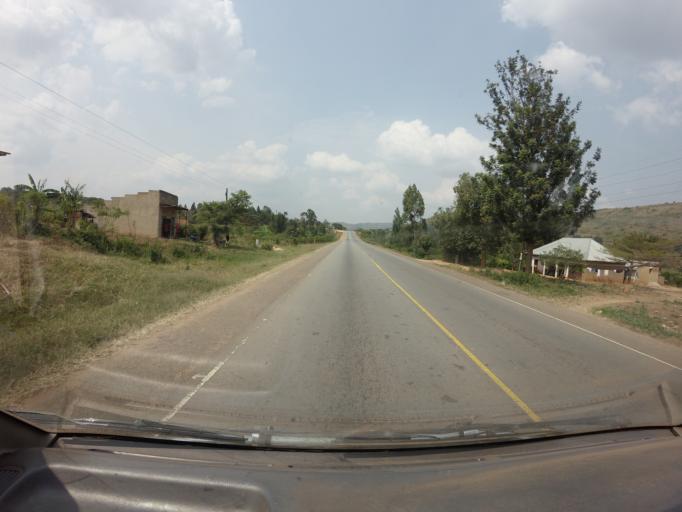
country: UG
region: Central Region
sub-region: Lyantonde District
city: Lyantonde
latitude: -0.3815
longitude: 31.2337
